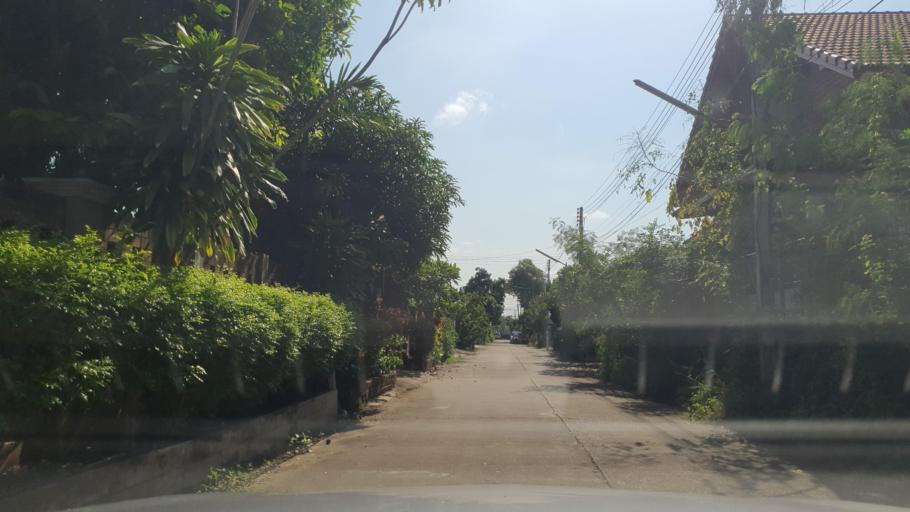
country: TH
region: Chiang Mai
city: Hang Dong
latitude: 18.7221
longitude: 98.9356
